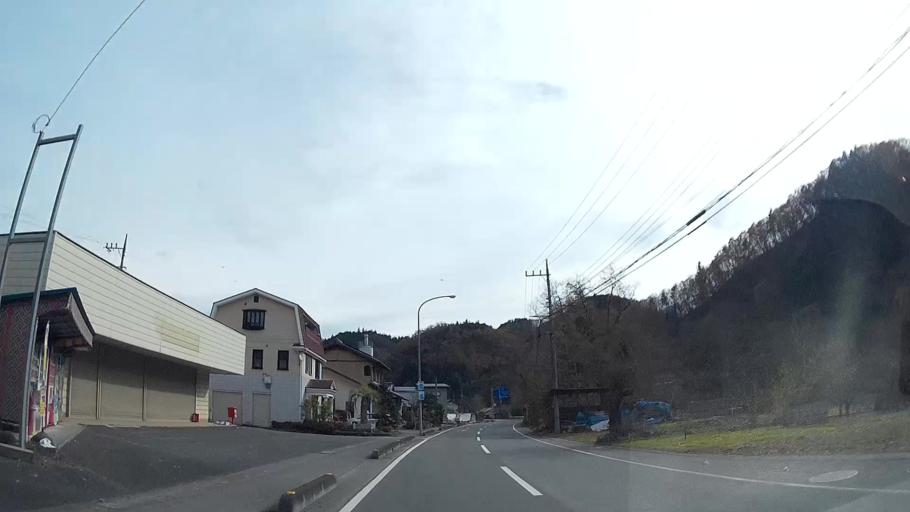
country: JP
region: Saitama
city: Chichibu
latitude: 36.0446
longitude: 138.9944
